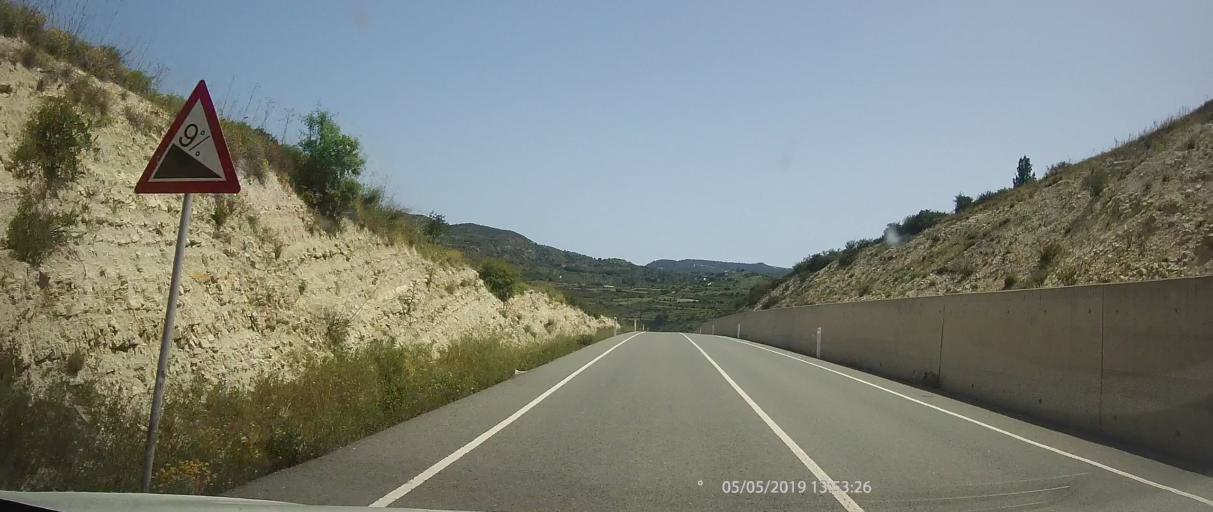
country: CY
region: Limassol
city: Pachna
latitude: 34.8208
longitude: 32.7245
